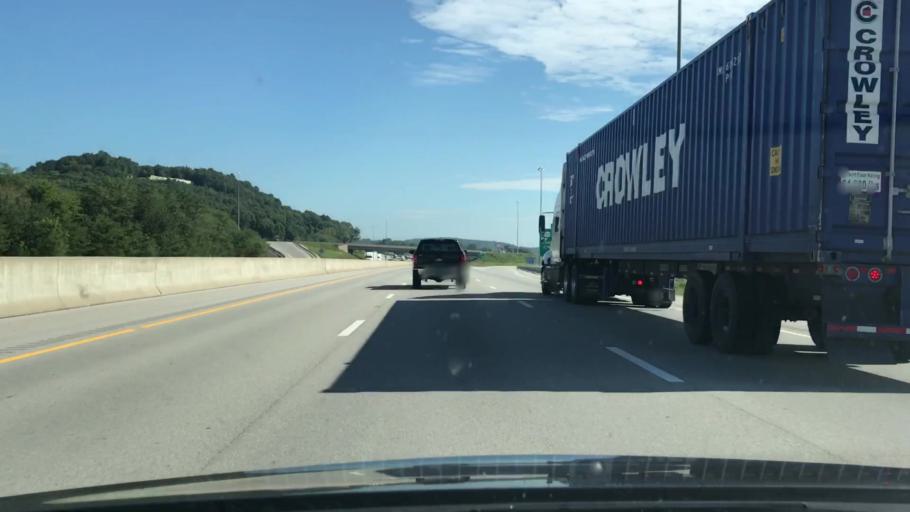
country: US
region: Kentucky
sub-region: Barren County
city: Cave City
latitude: 37.1323
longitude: -85.9814
